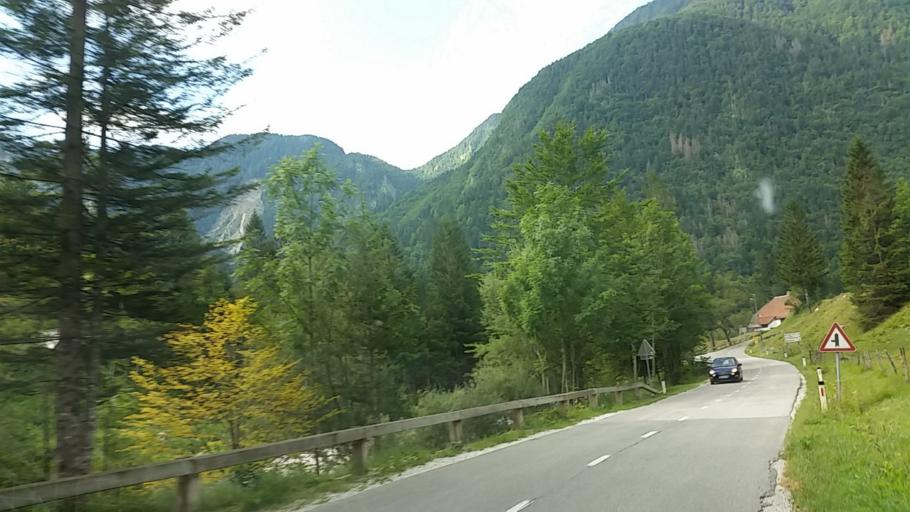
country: SI
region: Bovec
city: Bovec
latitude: 46.3427
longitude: 13.6849
